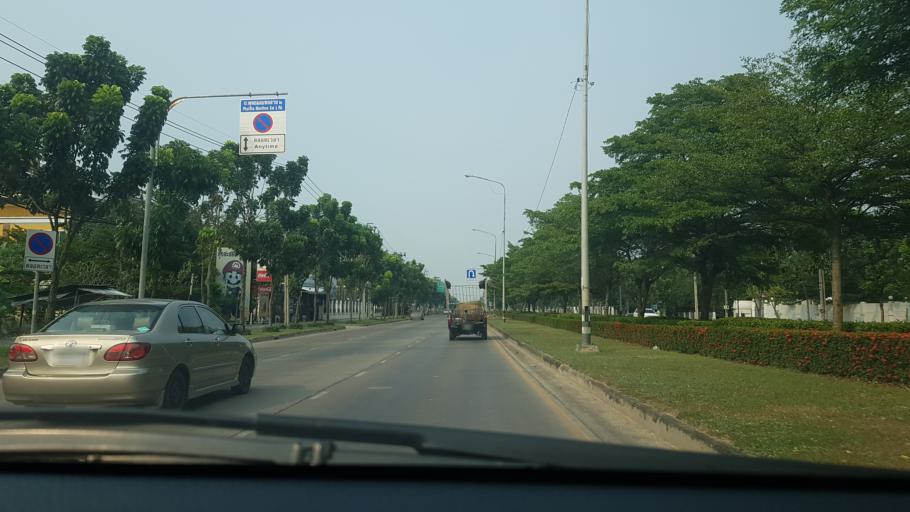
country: TH
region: Bangkok
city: Taling Chan
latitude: 13.7631
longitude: 100.3950
